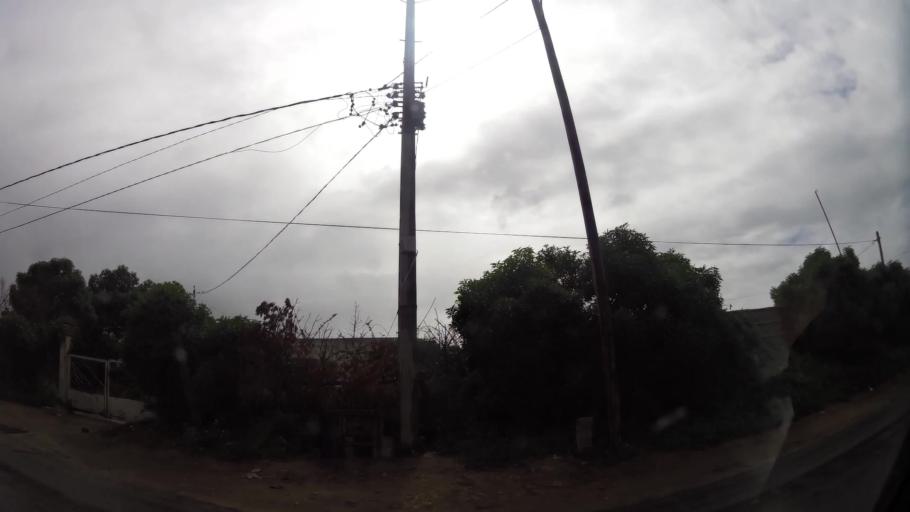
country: MA
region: Grand Casablanca
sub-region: Mediouna
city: Tit Mellil
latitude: 33.6399
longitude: -7.4753
